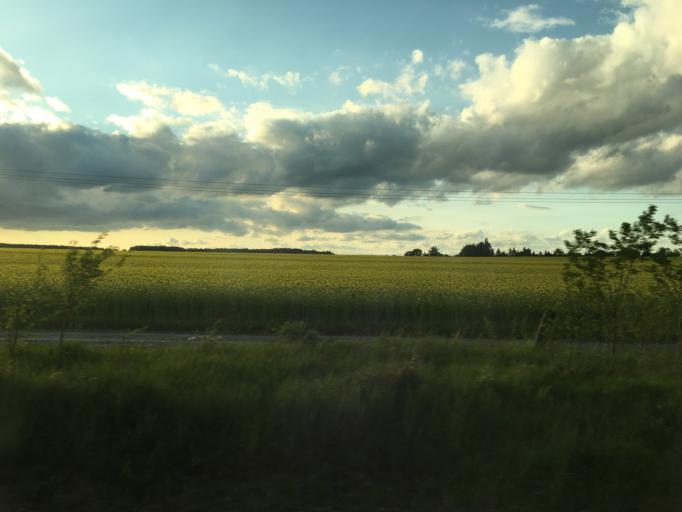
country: DE
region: Brandenburg
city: Hohenleipisch
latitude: 51.4794
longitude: 13.5399
